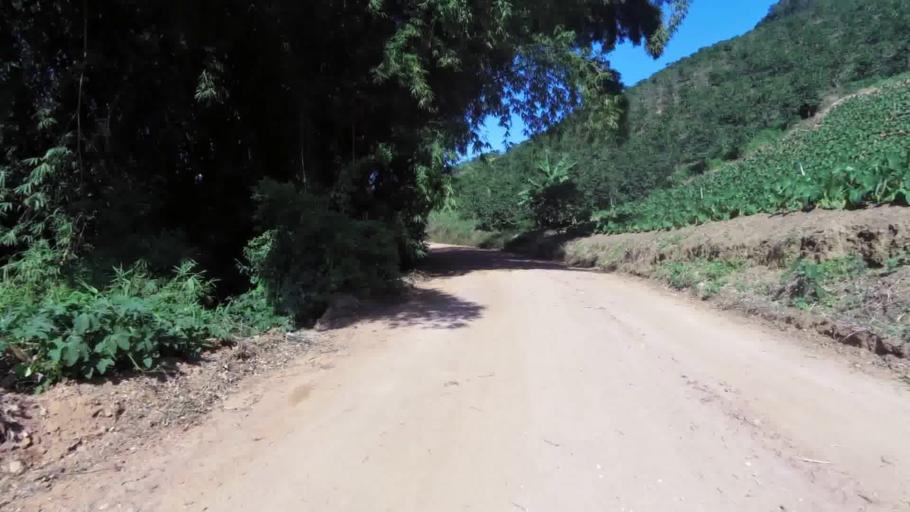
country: BR
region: Espirito Santo
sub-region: Alfredo Chaves
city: Alfredo Chaves
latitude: -20.5332
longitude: -40.8473
